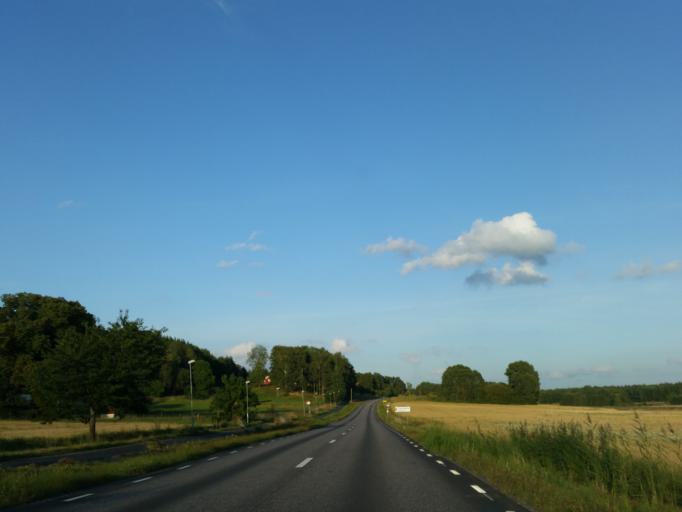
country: SE
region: Stockholm
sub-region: Nykvarns Kommun
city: Nykvarn
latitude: 59.2533
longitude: 17.5027
